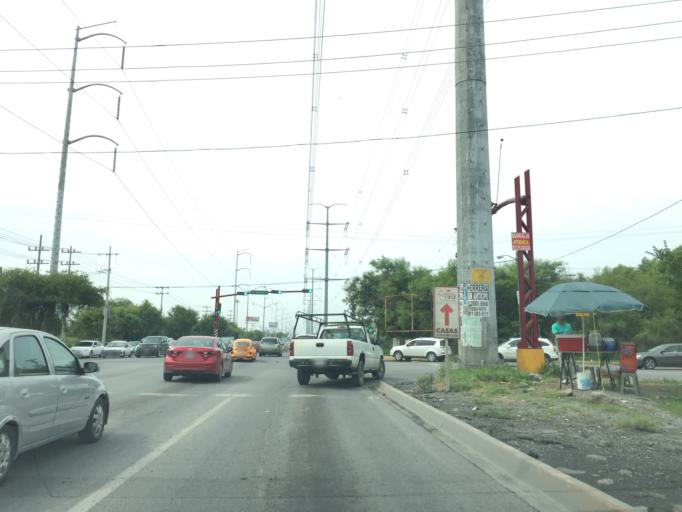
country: MX
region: Nuevo Leon
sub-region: Apodaca
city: Fraccionamiento Cosmopolis Octavo Sector
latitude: 25.7958
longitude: -100.2236
